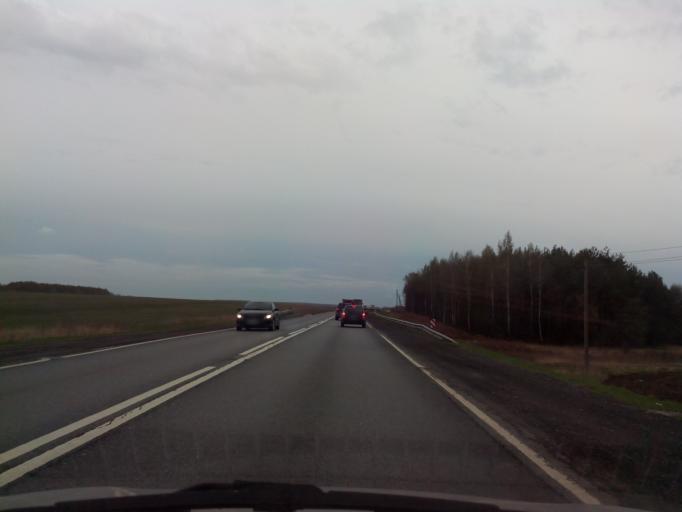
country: RU
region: Moskovskaya
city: Ozherel'ye
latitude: 54.6959
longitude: 38.3121
